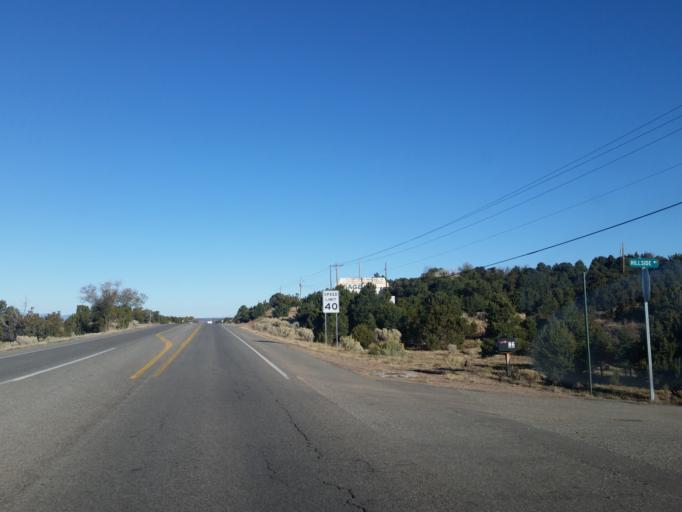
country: US
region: New Mexico
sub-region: Santa Fe County
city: Santa Fe
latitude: 35.6281
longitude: -105.9220
